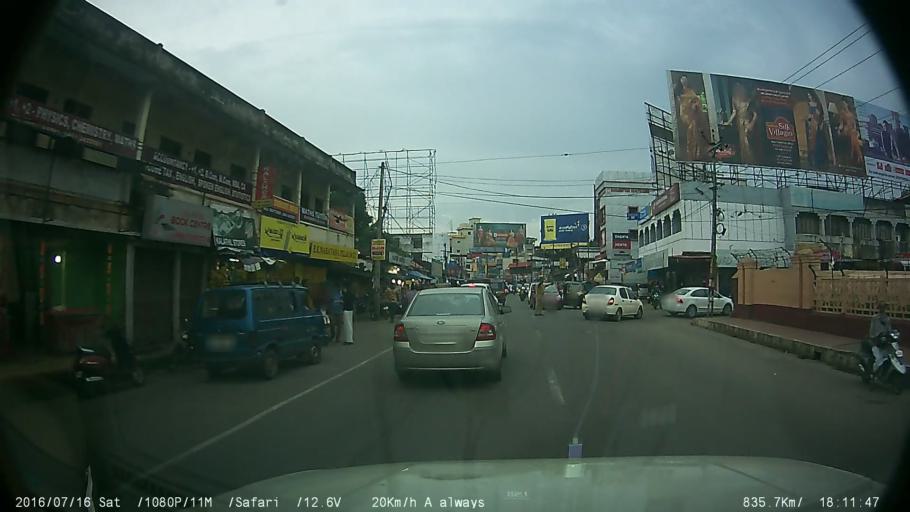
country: IN
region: Kerala
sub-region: Kottayam
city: Changanacheri
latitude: 9.4411
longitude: 76.5441
